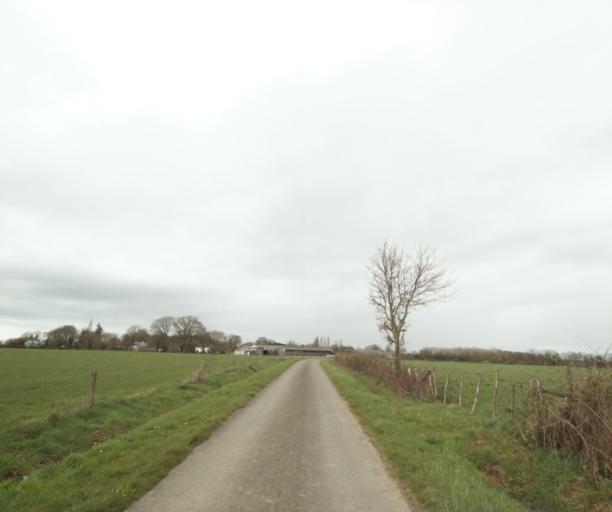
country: FR
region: Pays de la Loire
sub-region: Departement de la Loire-Atlantique
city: Bouvron
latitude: 47.4318
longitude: -1.8469
